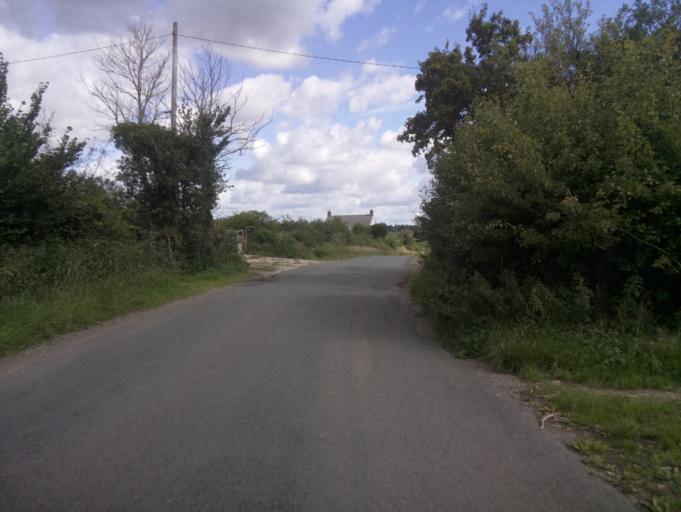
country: GB
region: England
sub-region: Gloucestershire
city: Newent
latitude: 51.8578
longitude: -2.3533
